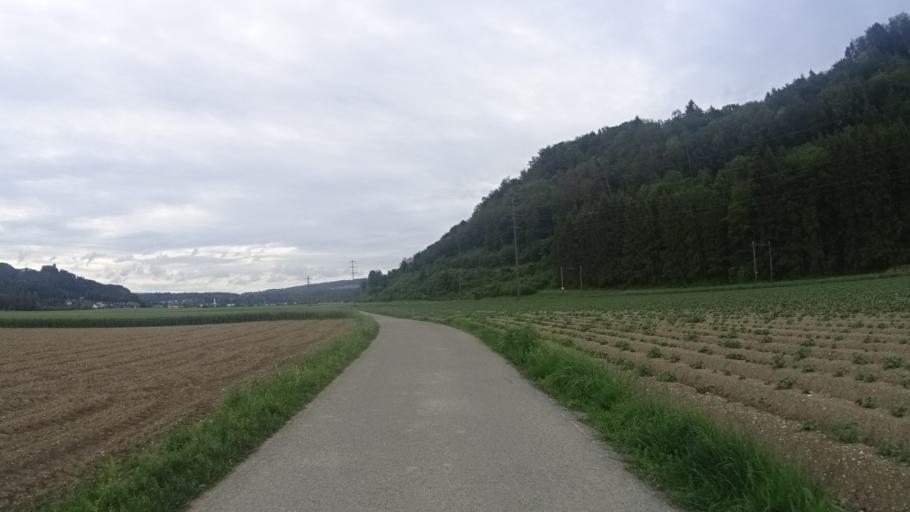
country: DE
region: Baden-Wuerttemberg
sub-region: Freiburg Region
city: Waldshut-Tiengen
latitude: 47.6128
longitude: 8.2077
